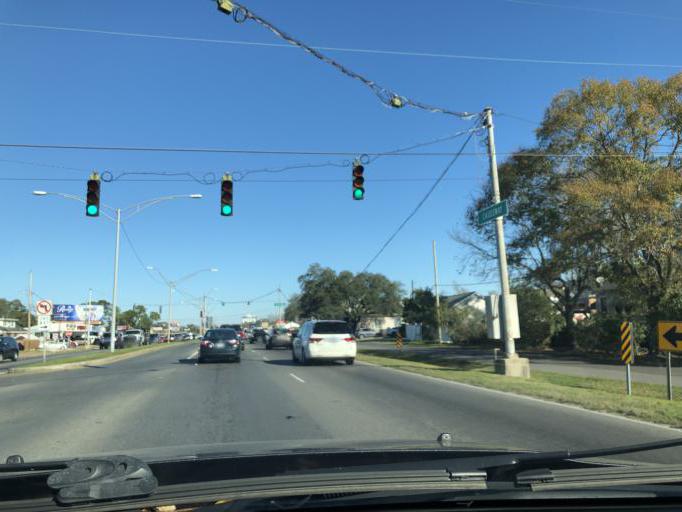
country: US
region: Louisiana
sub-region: Jefferson Parish
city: Metairie
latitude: 29.9811
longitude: -90.1560
